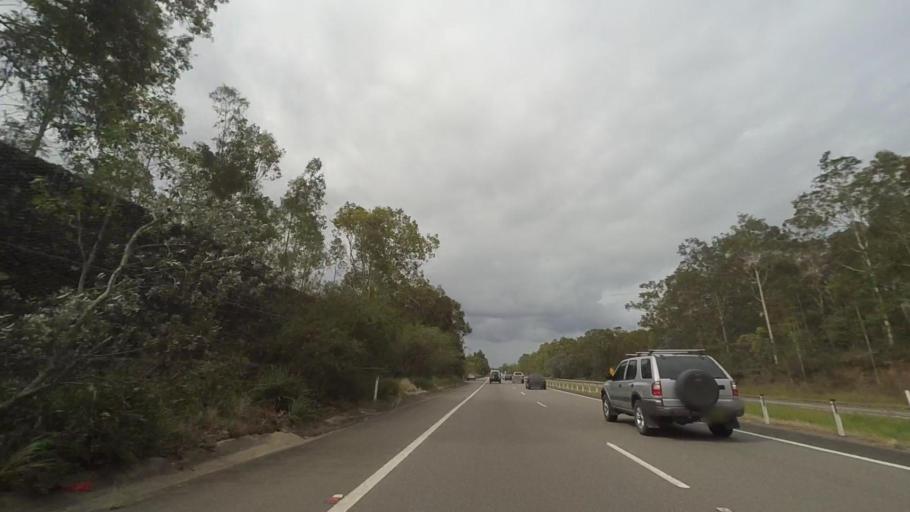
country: AU
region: New South Wales
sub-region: Port Stephens Shire
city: Raymond Terrace
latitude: -32.7367
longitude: 151.7795
